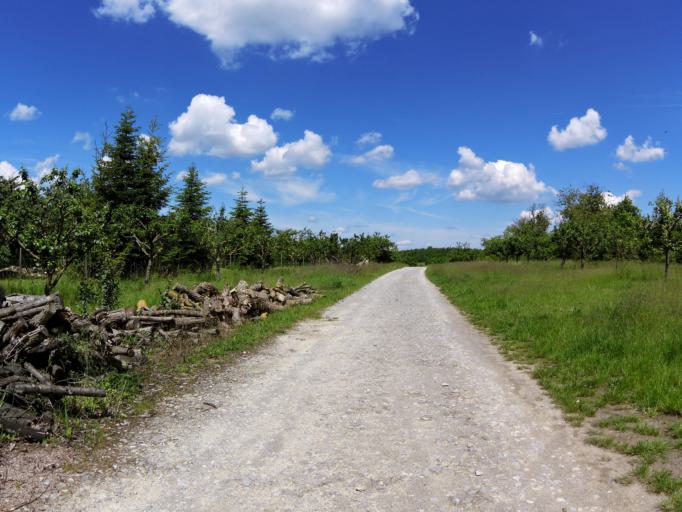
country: DE
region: Bavaria
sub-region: Regierungsbezirk Unterfranken
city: Winterhausen
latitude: 49.7270
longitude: 10.0226
